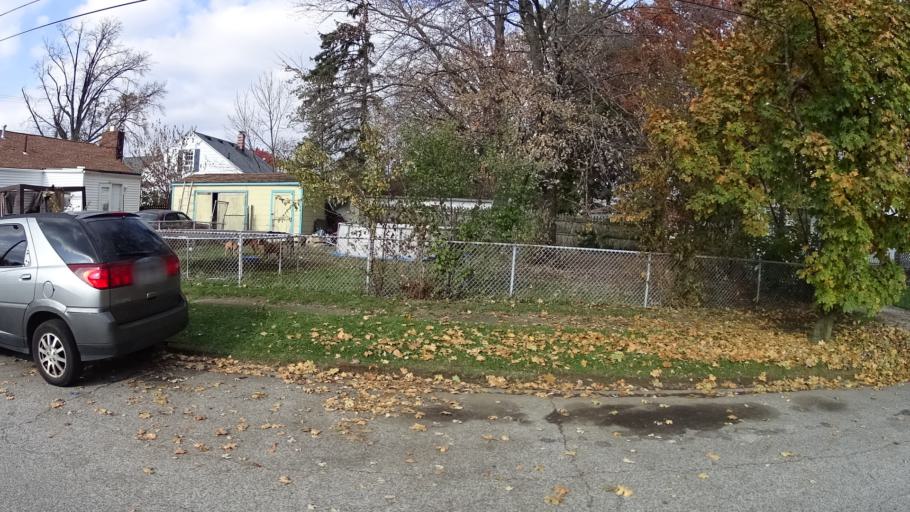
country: US
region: Ohio
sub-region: Lorain County
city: Elyria
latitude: 41.3797
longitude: -82.0939
